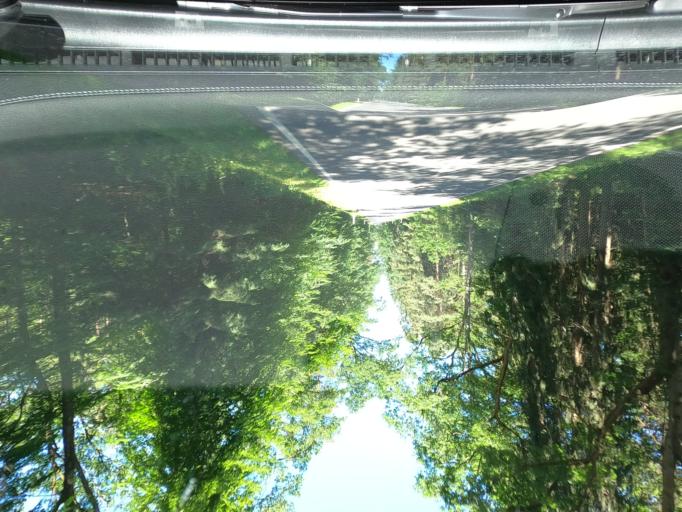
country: DE
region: Lower Saxony
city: Wathlingen
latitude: 52.5115
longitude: 10.1363
